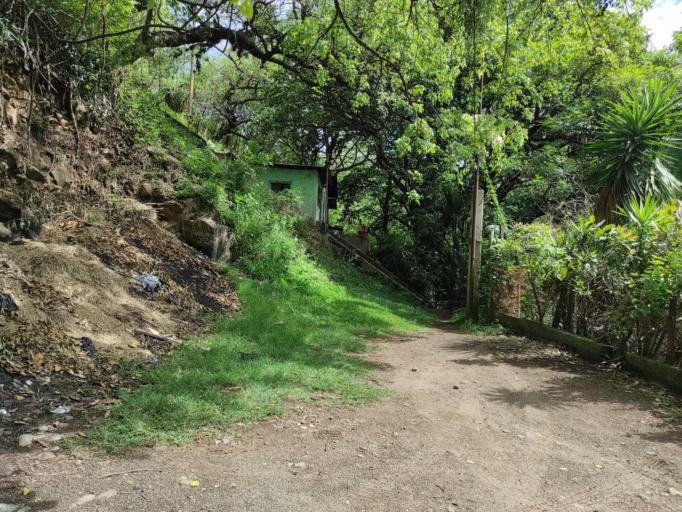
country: GT
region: Guatemala
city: Amatitlan
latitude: 14.4839
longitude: -90.6107
